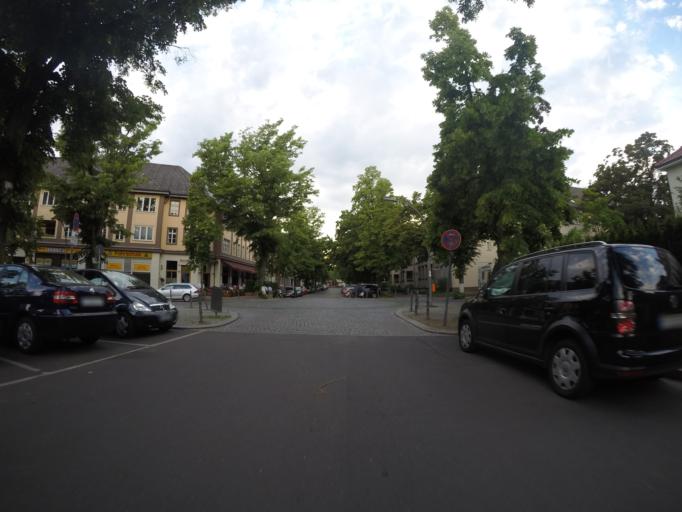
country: DE
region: Berlin
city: Schmargendorf
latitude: 52.4773
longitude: 13.2906
